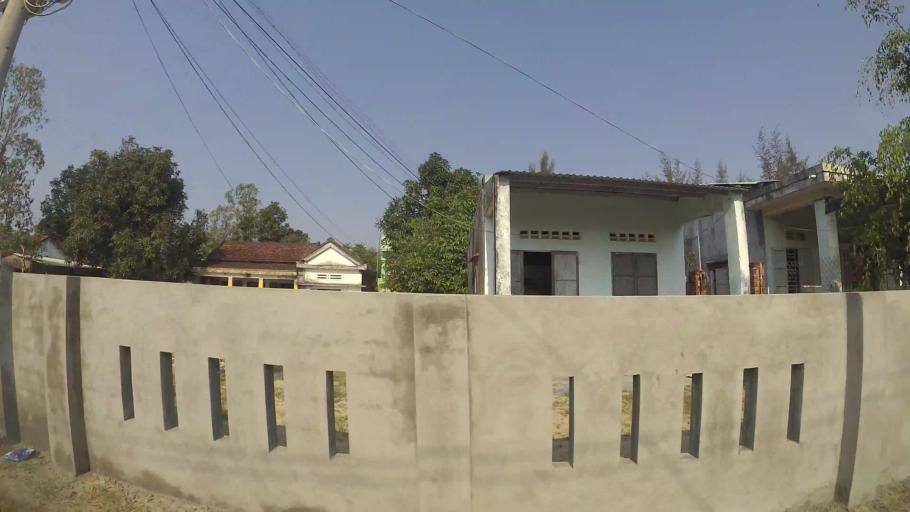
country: VN
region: Da Nang
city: Ngu Hanh Son
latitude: 15.9588
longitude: 108.2640
